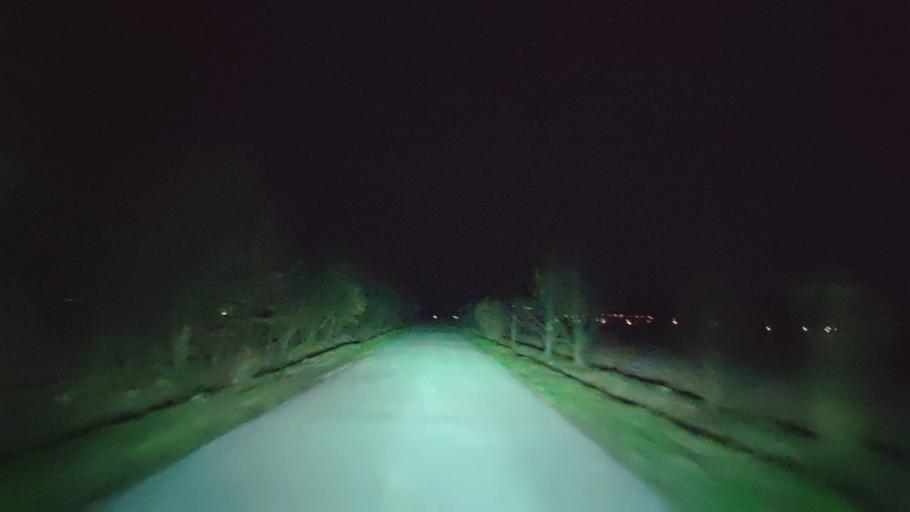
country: HU
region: Borsod-Abauj-Zemplen
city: Satoraljaujhely
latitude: 48.4637
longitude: 21.6045
